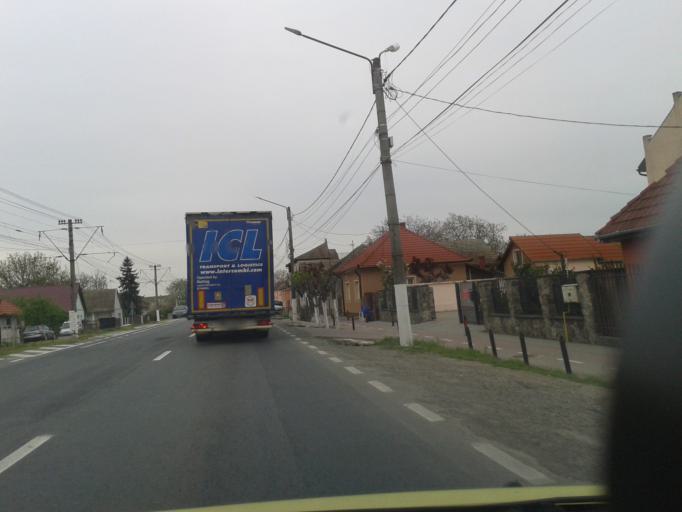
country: RO
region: Arad
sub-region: Comuna Vladimirescu
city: Vladimirescu
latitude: 46.1626
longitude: 21.4074
